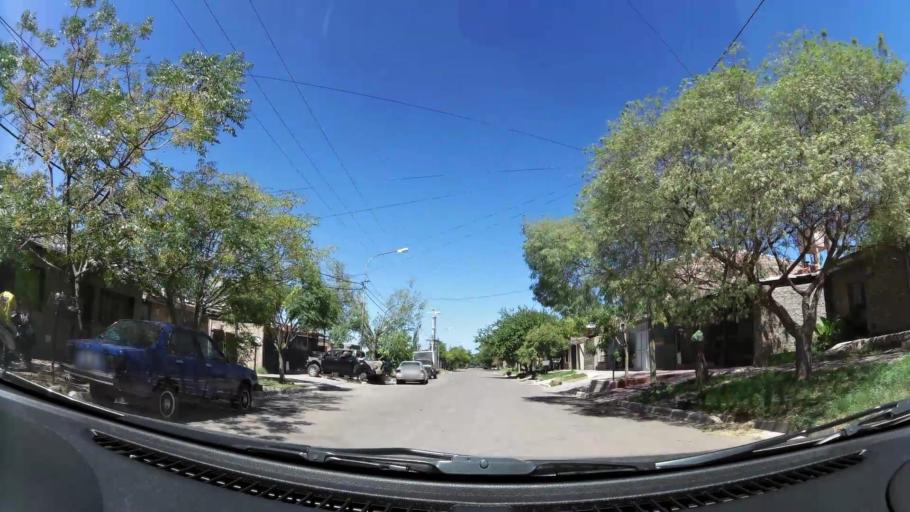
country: AR
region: Mendoza
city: Las Heras
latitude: -32.8504
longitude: -68.8650
